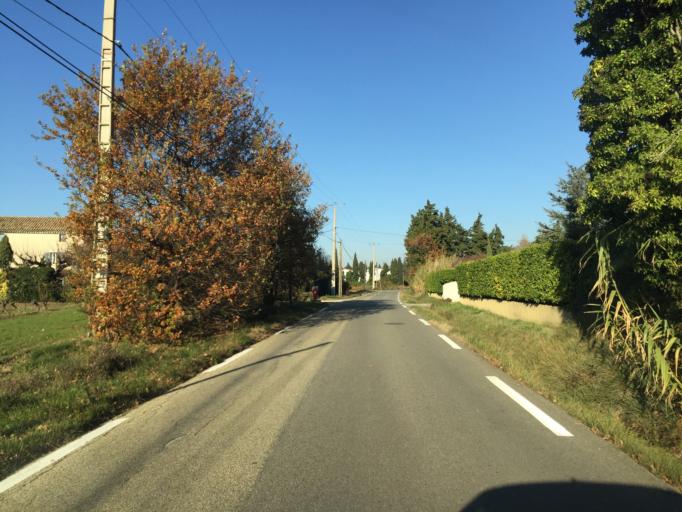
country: FR
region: Provence-Alpes-Cote d'Azur
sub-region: Departement du Vaucluse
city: Camaret-sur-Aigues
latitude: 44.1723
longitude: 4.8791
